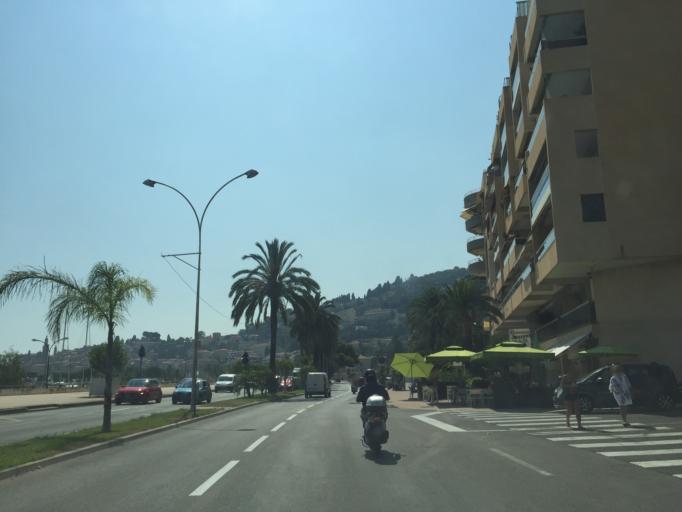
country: FR
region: Provence-Alpes-Cote d'Azur
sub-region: Departement des Alpes-Maritimes
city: Menton
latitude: 43.7840
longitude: 7.5169
